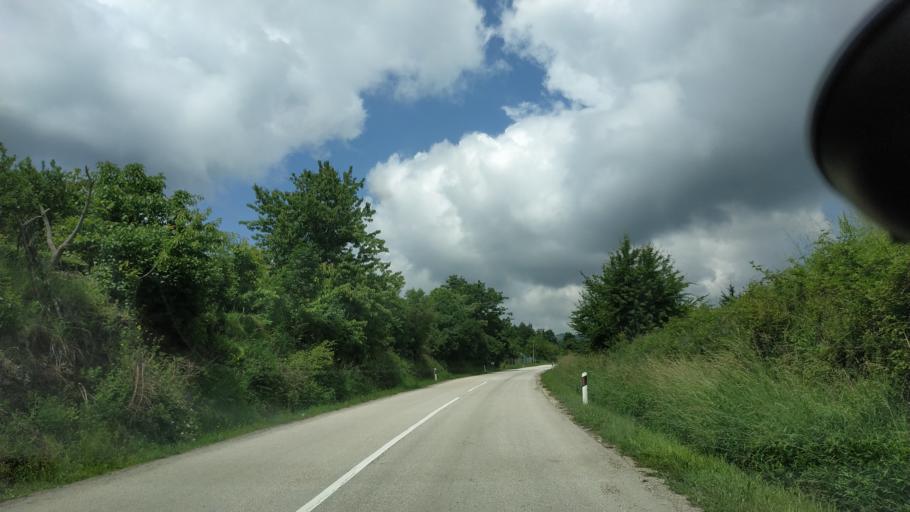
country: RS
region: Central Serbia
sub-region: Borski Okrug
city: Bor
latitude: 44.0840
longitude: 22.0090
